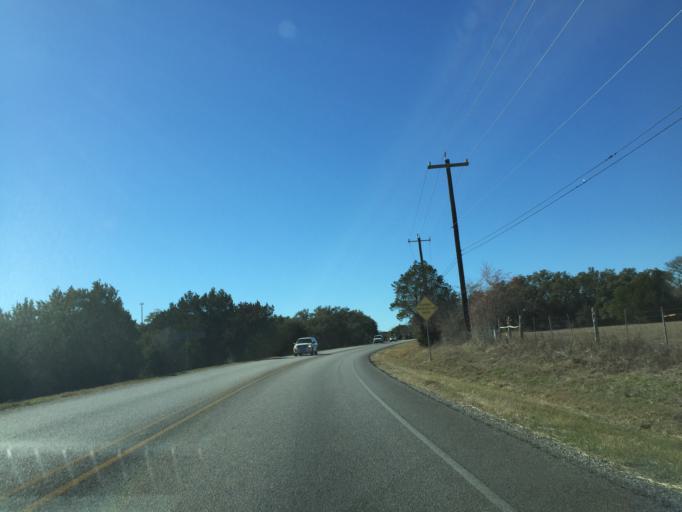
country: US
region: Texas
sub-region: Comal County
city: Bulverde
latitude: 29.7427
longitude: -98.4278
